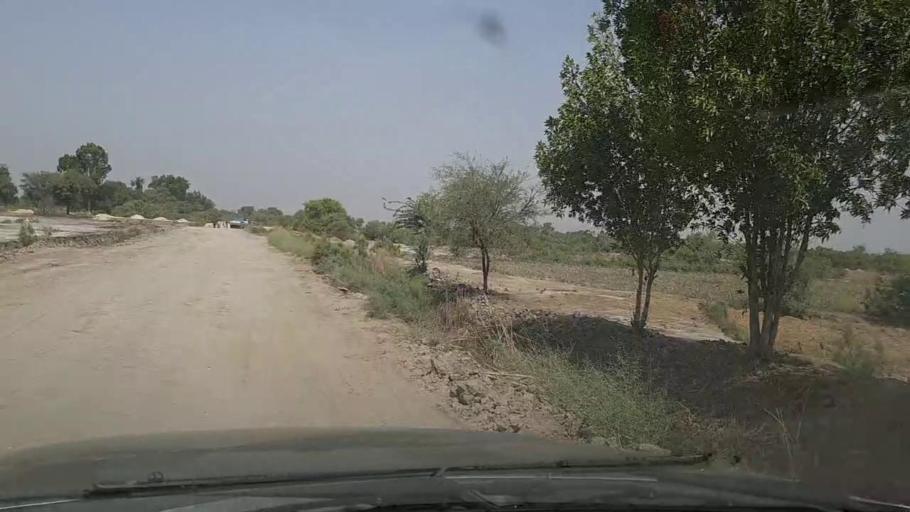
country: PK
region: Sindh
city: Thul
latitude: 28.3993
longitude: 68.7095
